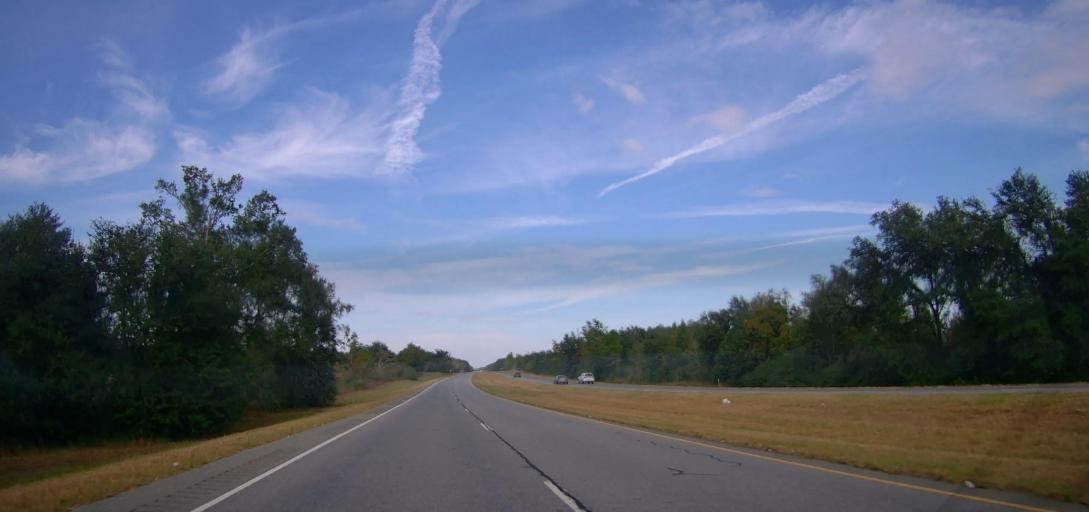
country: US
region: Georgia
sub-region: Mitchell County
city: Camilla
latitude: 31.2899
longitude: -84.1854
